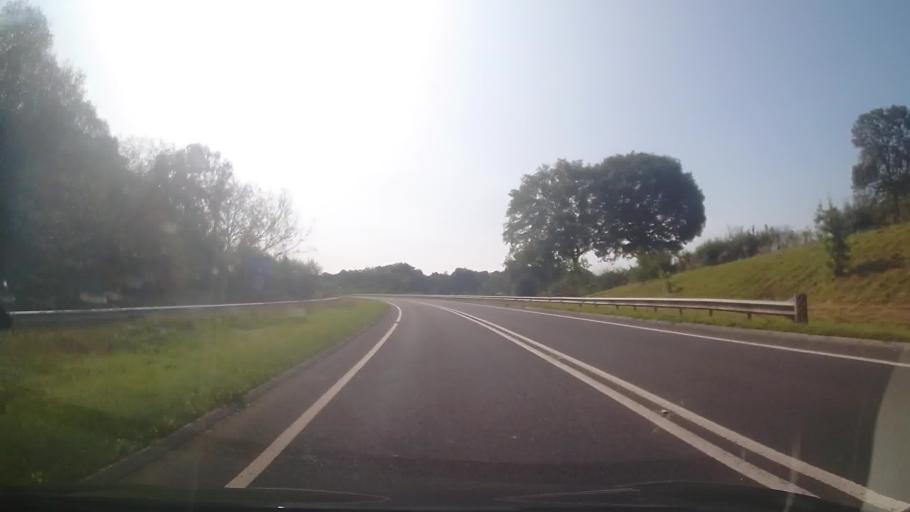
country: GB
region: Wales
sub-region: Sir Powys
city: Builth Wells
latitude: 52.1969
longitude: -3.4375
